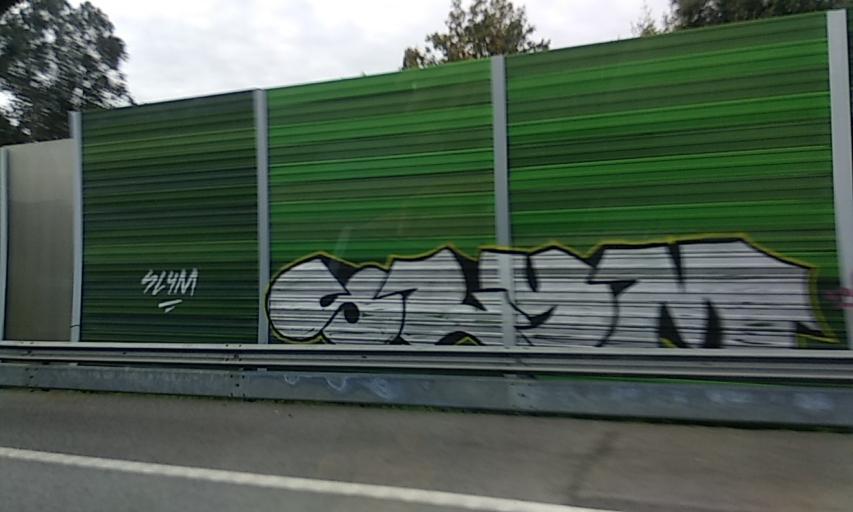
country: PT
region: Porto
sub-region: Santo Tirso
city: Santo Tirso
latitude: 41.3687
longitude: -8.5029
